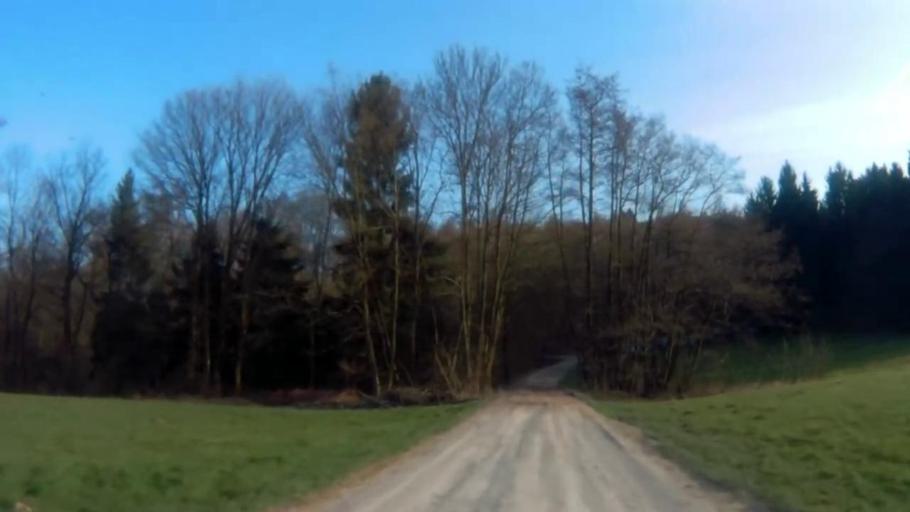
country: DE
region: Hesse
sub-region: Regierungsbezirk Darmstadt
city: Frankisch-Crumbach
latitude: 49.7456
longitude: 8.8218
